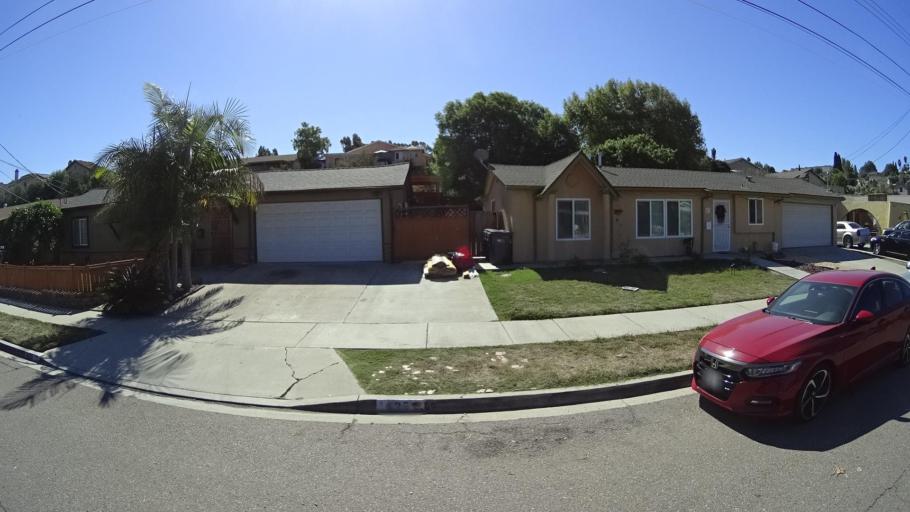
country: US
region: California
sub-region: San Diego County
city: La Presa
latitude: 32.7017
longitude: -117.0158
